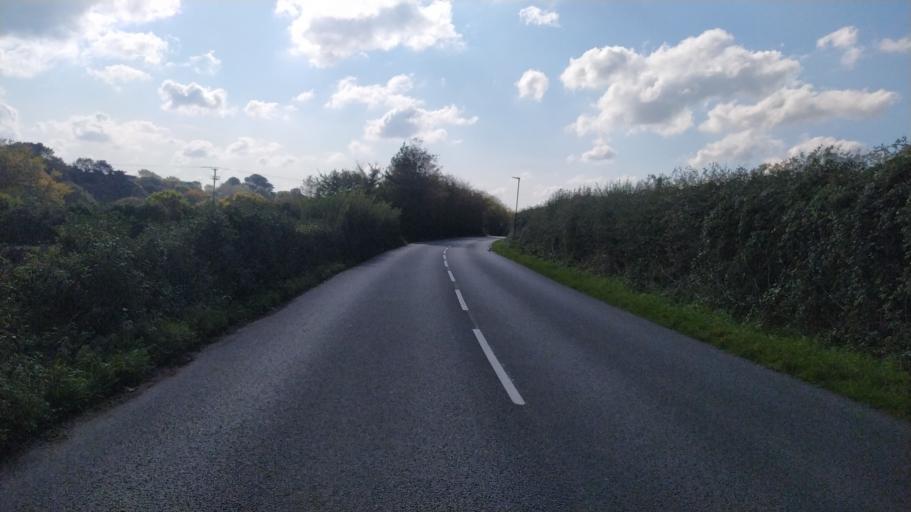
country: GB
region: England
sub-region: Isle of Wight
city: Freshwater
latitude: 50.6936
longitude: -1.5229
